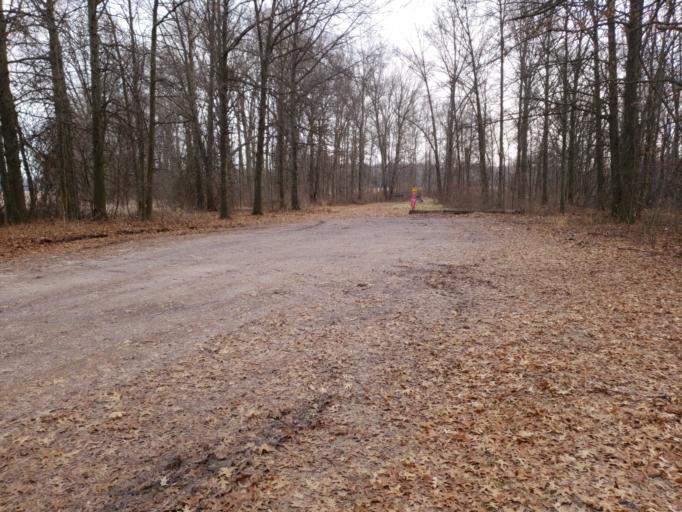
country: US
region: Ohio
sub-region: Stark County
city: Alliance
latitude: 41.0028
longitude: -81.0985
